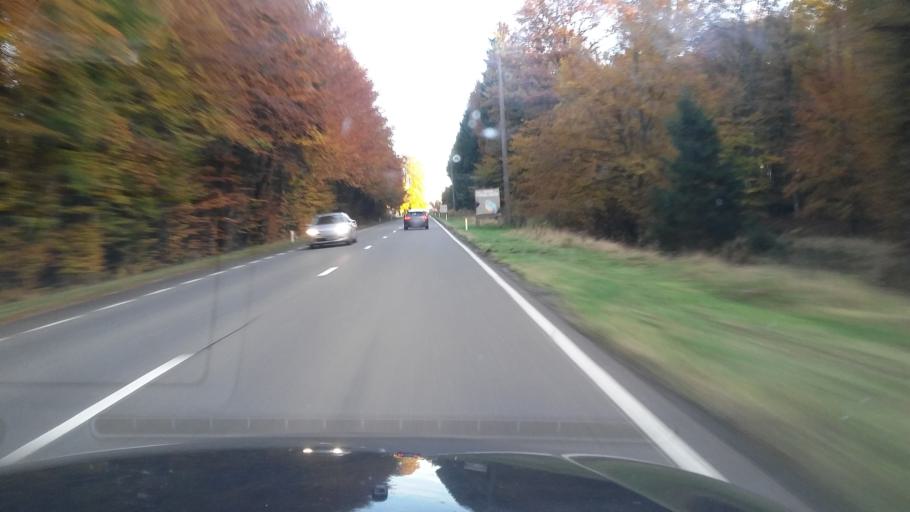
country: BE
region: Wallonia
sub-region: Province du Luxembourg
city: Herbeumont
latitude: 49.7556
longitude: 5.1589
